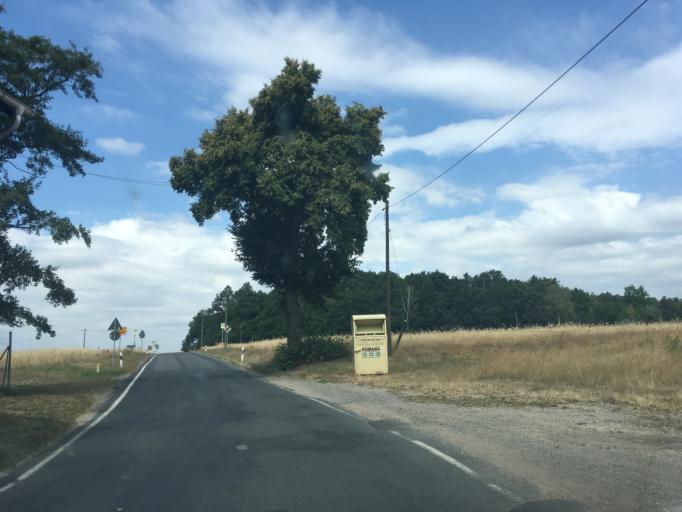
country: DE
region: Saxony
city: Tauscha
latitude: 51.2485
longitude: 13.7812
